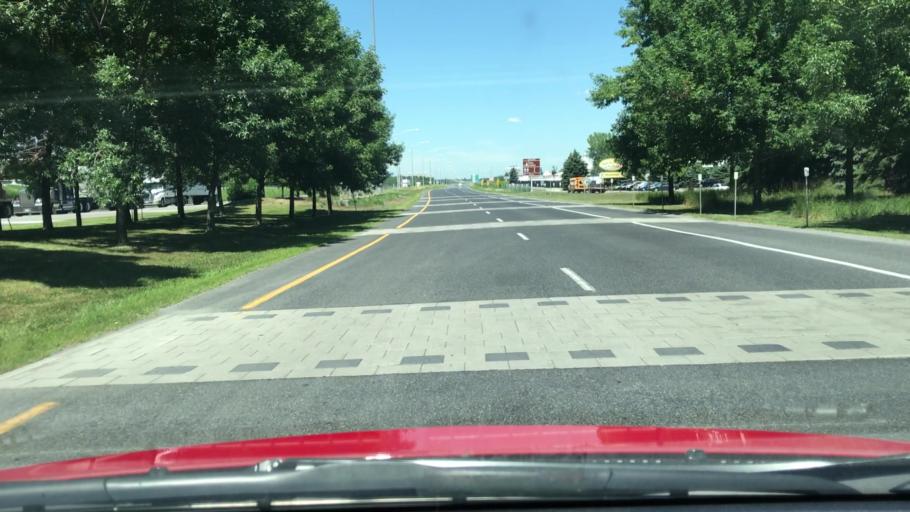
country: US
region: New York
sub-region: Clinton County
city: Champlain
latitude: 45.0121
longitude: -73.4524
